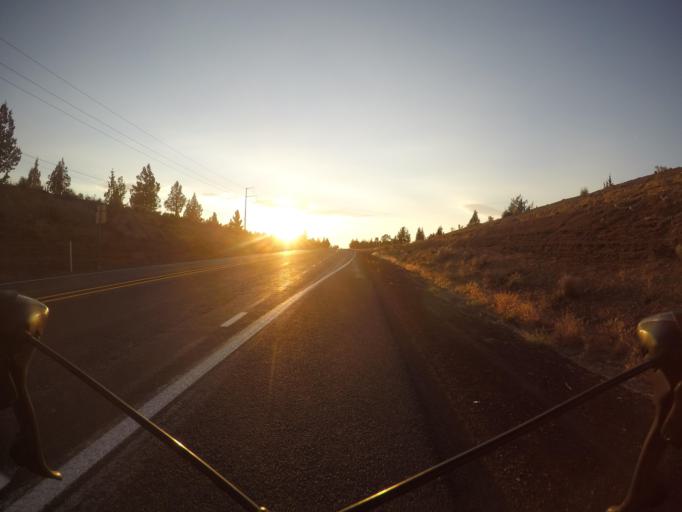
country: US
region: Oregon
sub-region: Deschutes County
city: Redmond
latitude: 44.2757
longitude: -121.2623
